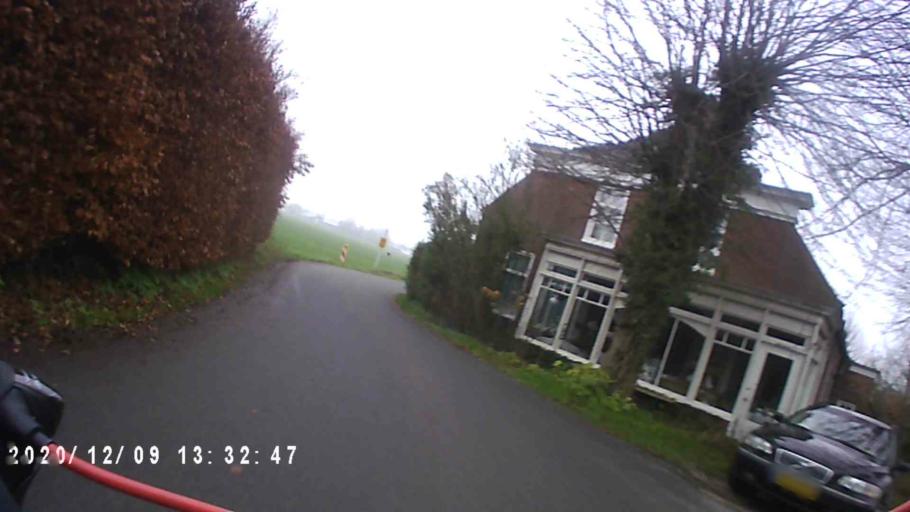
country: NL
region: Groningen
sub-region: Gemeente Bedum
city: Bedum
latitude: 53.2782
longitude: 6.6015
